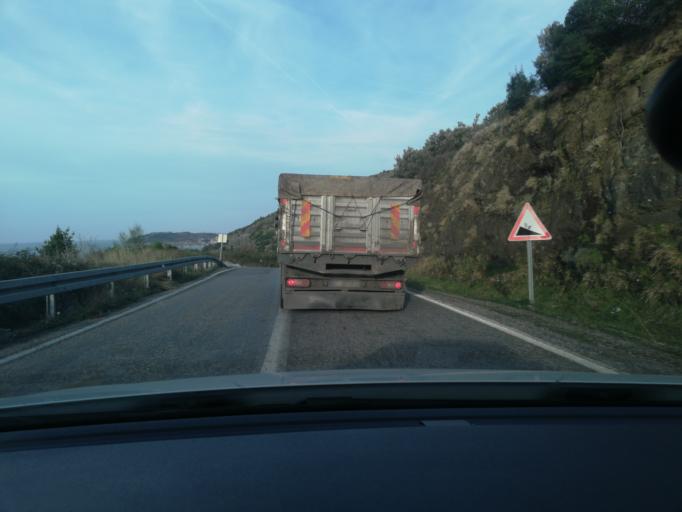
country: TR
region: Zonguldak
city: Tieum
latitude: 41.5476
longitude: 31.9988
